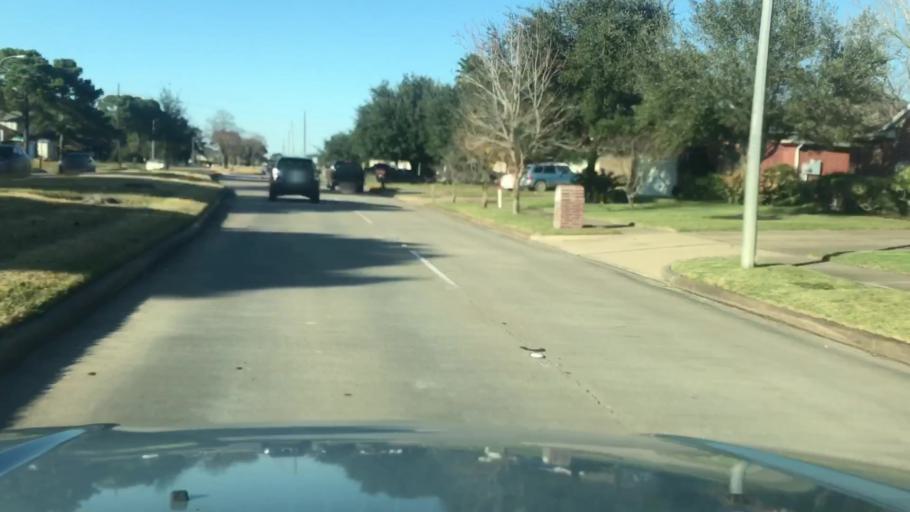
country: US
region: Texas
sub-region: Harris County
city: Katy
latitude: 29.8215
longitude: -95.7526
